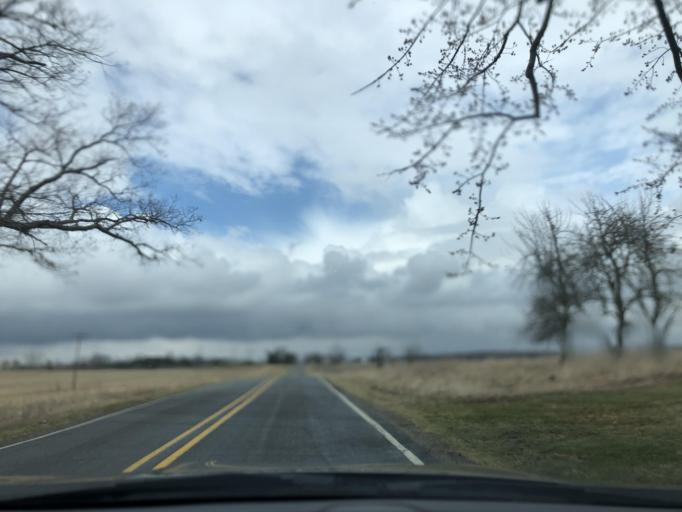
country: US
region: Michigan
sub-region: Clinton County
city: Saint Johns
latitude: 43.0642
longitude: -84.6108
